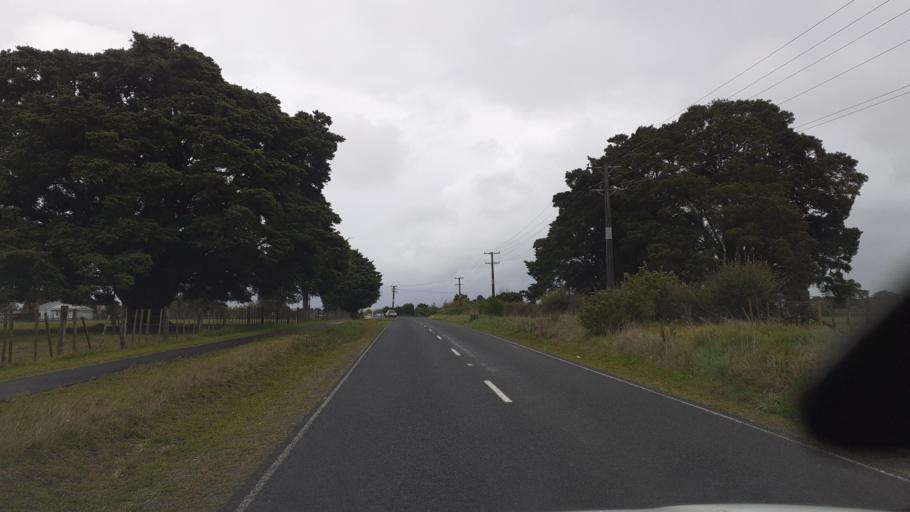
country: NZ
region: Northland
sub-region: Far North District
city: Waimate North
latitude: -35.4180
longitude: 173.7971
